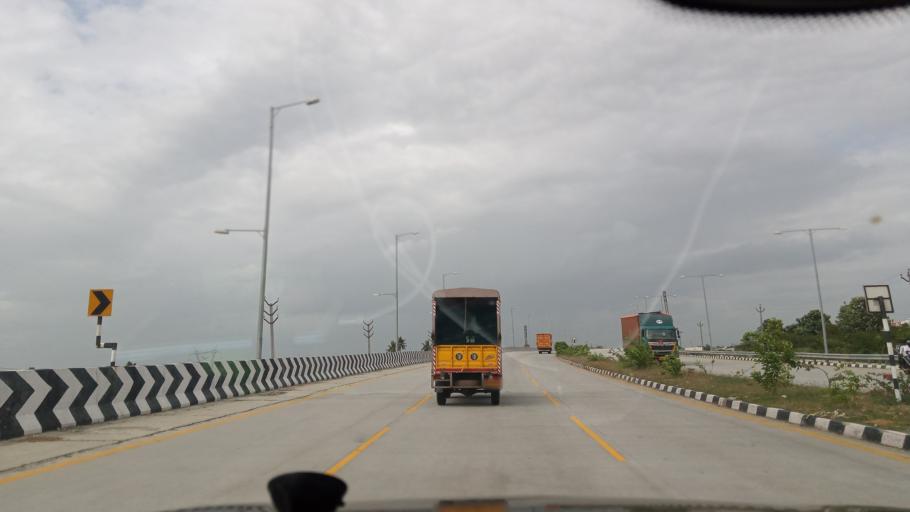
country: IN
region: Andhra Pradesh
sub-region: Chittoor
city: Palmaner
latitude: 13.2212
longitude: 78.7317
